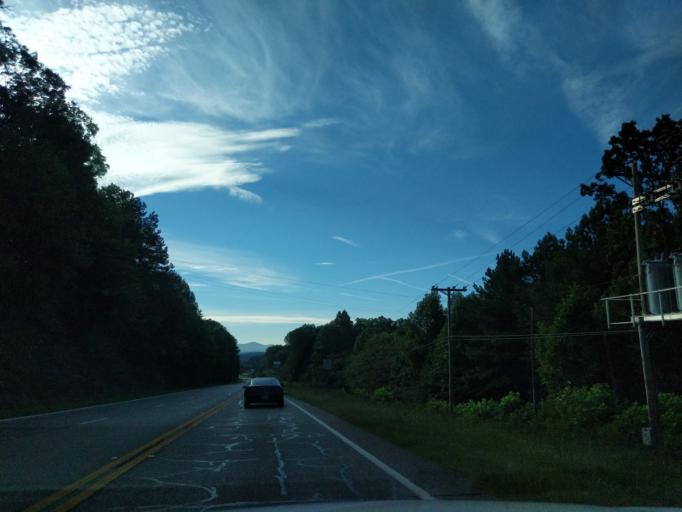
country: US
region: Georgia
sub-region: Fannin County
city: Blue Ridge
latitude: 34.9022
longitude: -84.3716
